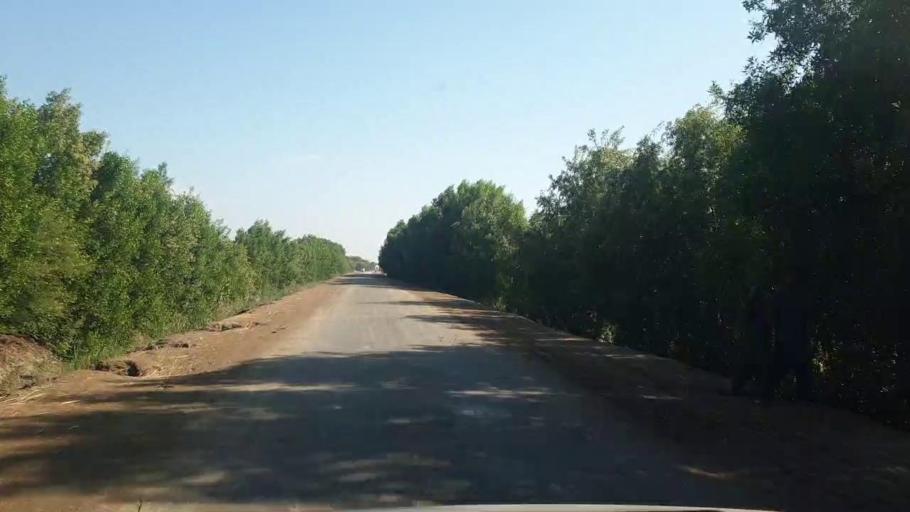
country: PK
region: Sindh
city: Rajo Khanani
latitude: 24.9189
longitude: 68.9250
